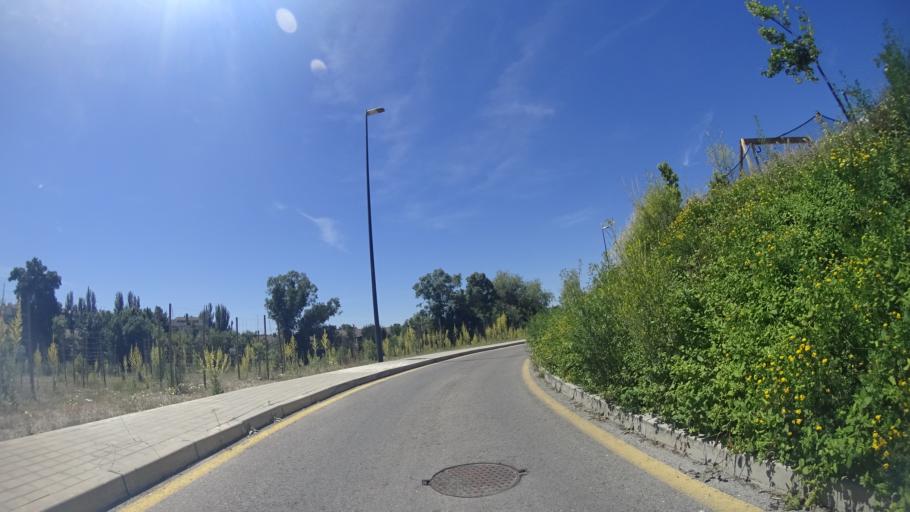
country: ES
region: Madrid
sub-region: Provincia de Madrid
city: Collado-Villalba
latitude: 40.6539
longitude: -4.0003
